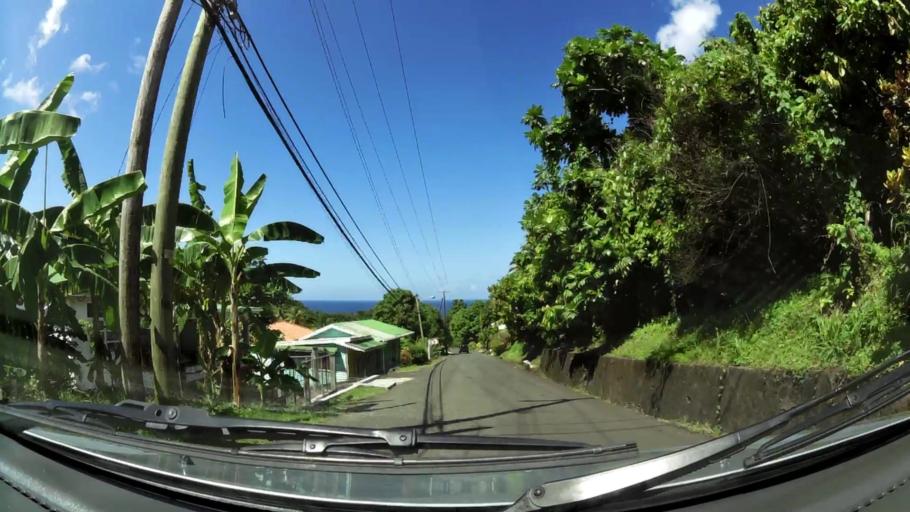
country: GD
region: Saint John
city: Gouyave
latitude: 12.1246
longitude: -61.7445
